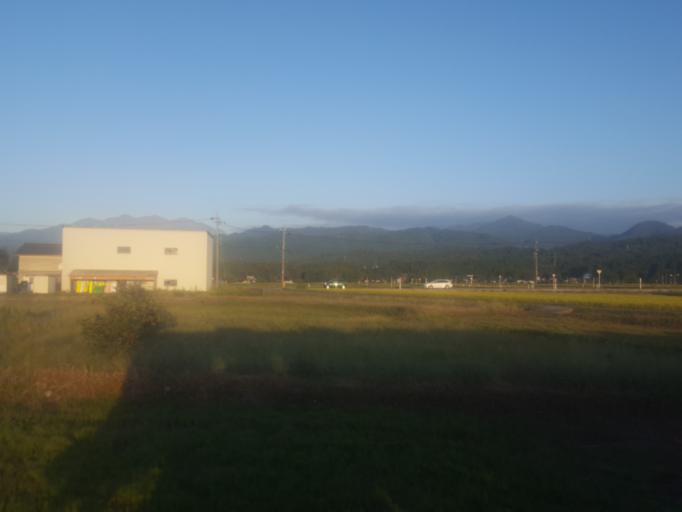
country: JP
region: Toyama
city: Kamiichi
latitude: 36.6272
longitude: 137.3215
